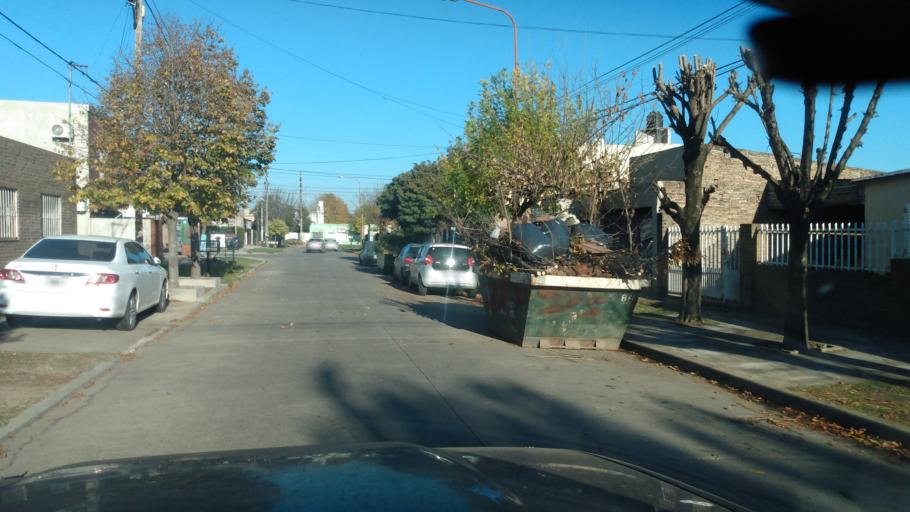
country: AR
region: Buenos Aires
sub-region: Partido de Lujan
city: Lujan
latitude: -34.5612
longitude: -59.0987
